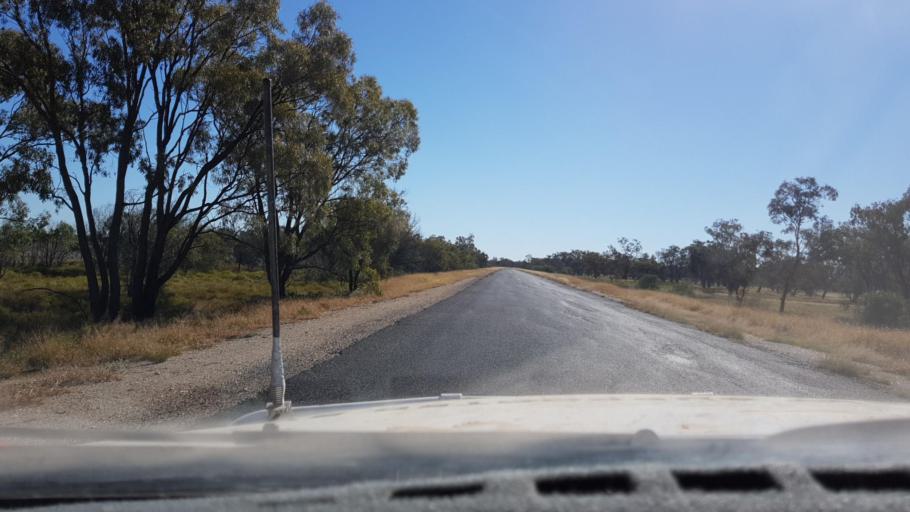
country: AU
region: New South Wales
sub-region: Walgett
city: Lightning Ridge
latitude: -29.5729
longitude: 148.6707
